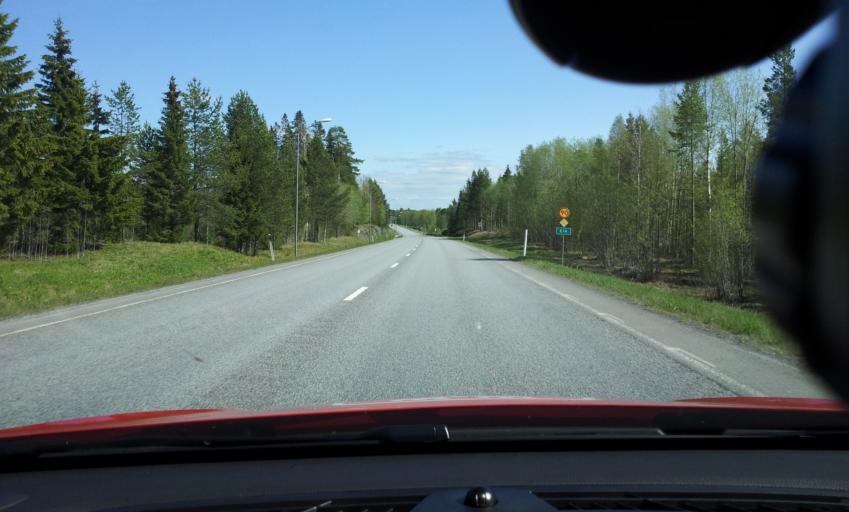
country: SE
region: Jaemtland
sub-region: Krokoms Kommun
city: Valla
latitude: 63.3248
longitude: 14.0499
